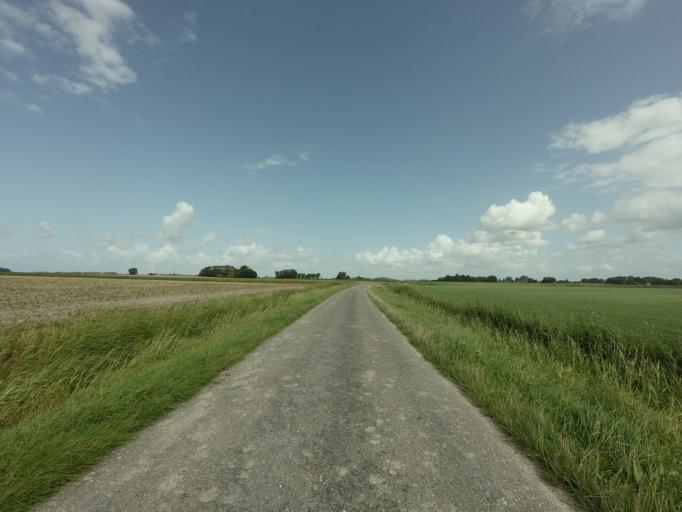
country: NL
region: Friesland
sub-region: Gemeente Harlingen
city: Harlingen
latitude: 53.1185
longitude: 5.4383
